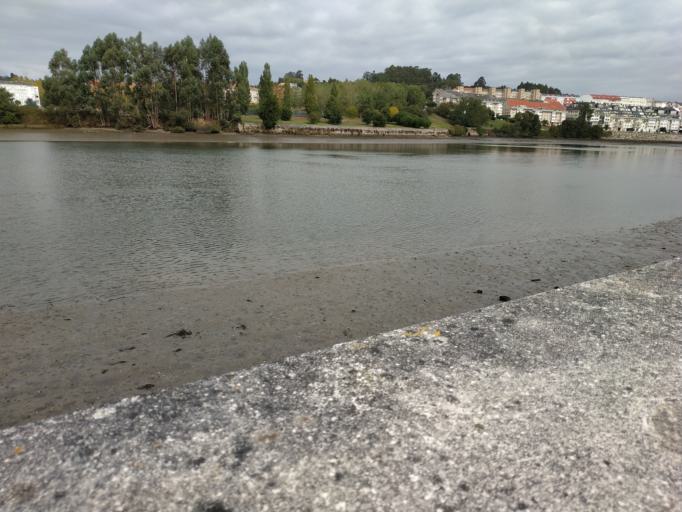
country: ES
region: Galicia
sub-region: Provincia da Coruna
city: Cambre
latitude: 43.3209
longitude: -8.3664
